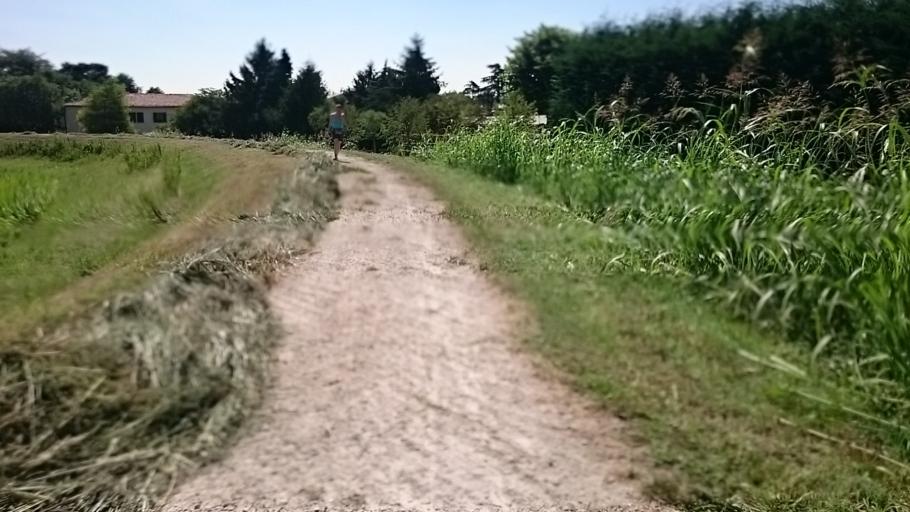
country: IT
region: Veneto
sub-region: Provincia di Padova
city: Saccolongo
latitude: 45.4053
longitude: 11.7486
